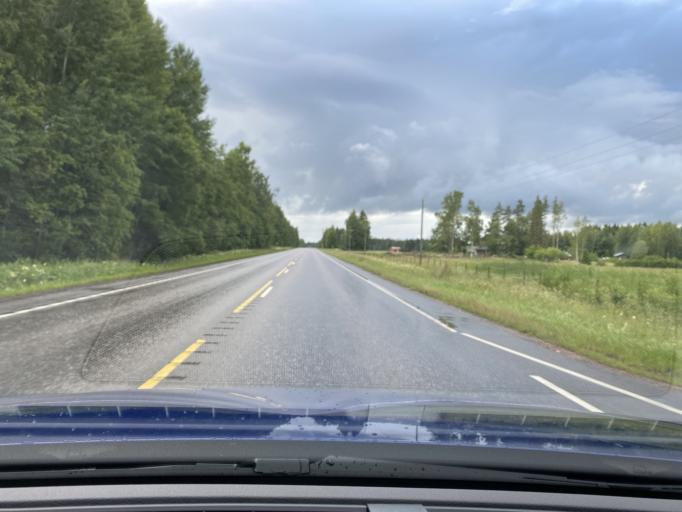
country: FI
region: Uusimaa
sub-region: Helsinki
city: Nurmijaervi
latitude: 60.5444
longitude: 24.8315
